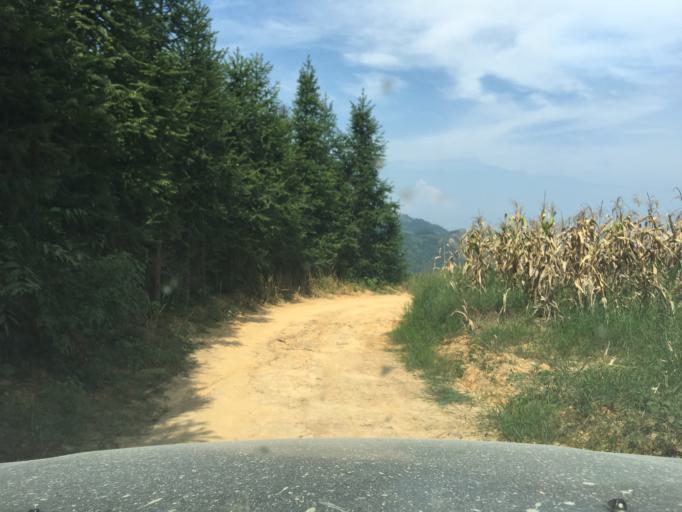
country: CN
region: Guangxi Zhuangzu Zizhiqu
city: Xinzhou
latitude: 25.0458
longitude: 105.8651
